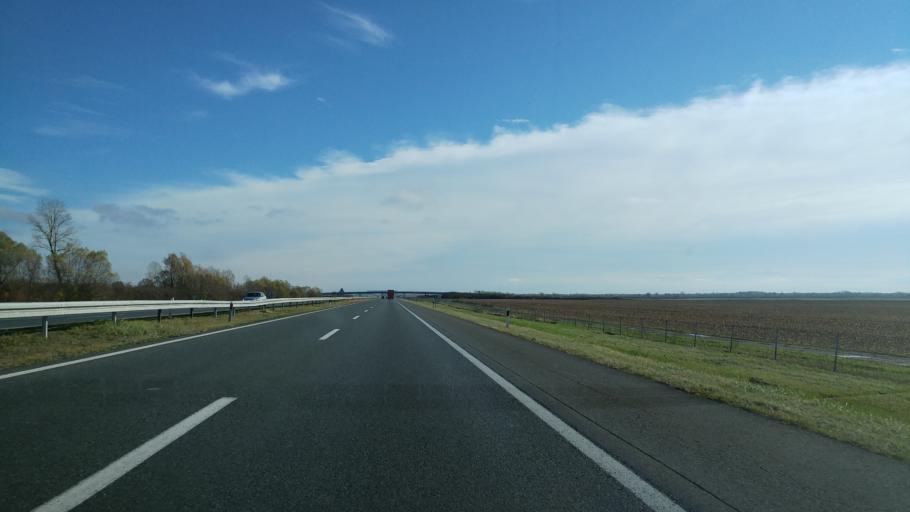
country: HR
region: Brodsko-Posavska
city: Okucani
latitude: 45.2803
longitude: 17.1173
